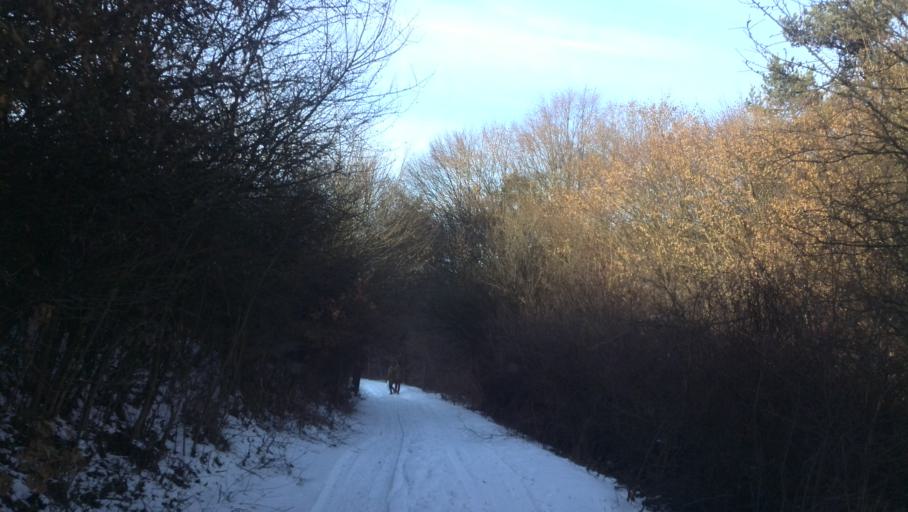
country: SK
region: Presovsky
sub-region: Okres Presov
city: Presov
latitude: 48.9635
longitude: 21.1078
